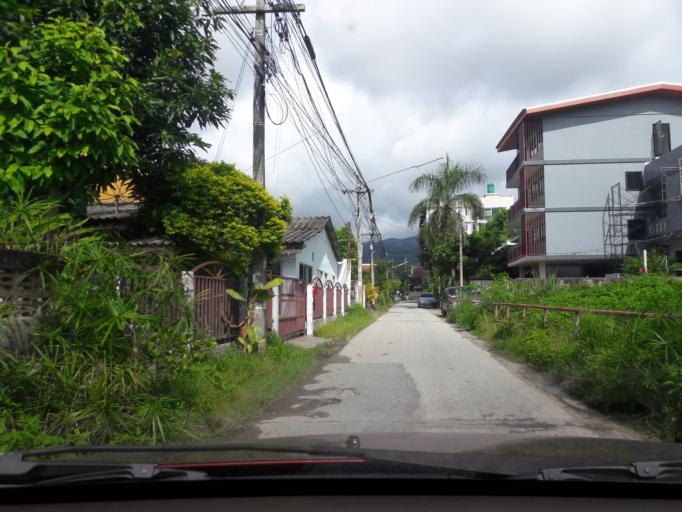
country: TH
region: Chiang Mai
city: Chiang Mai
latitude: 18.7852
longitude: 98.9695
